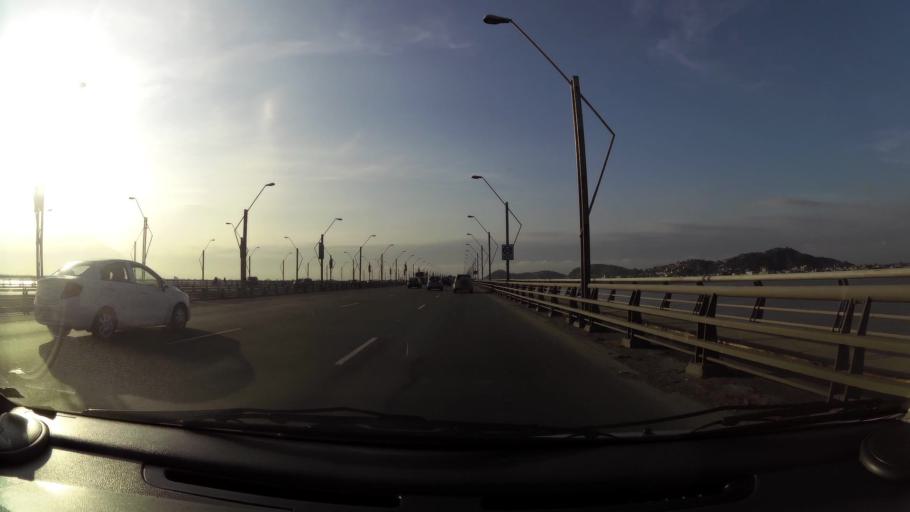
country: EC
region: Guayas
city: Eloy Alfaro
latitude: -2.1591
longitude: -79.8544
